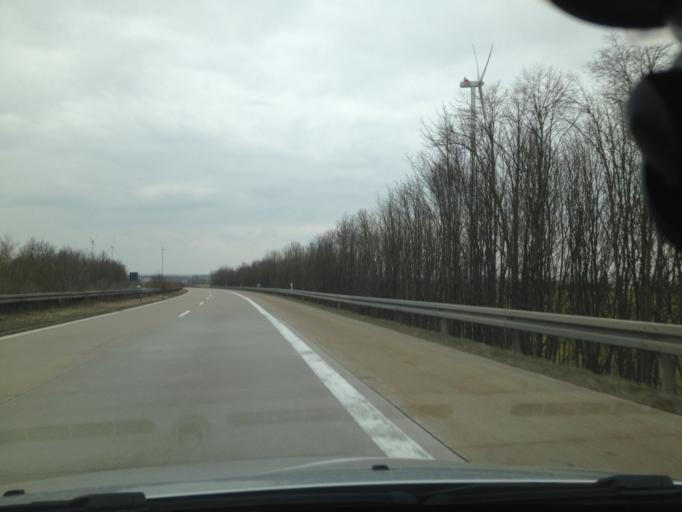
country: DE
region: Bavaria
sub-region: Regierungsbezirk Mittelfranken
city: Gollhofen
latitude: 49.5295
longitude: 10.1896
